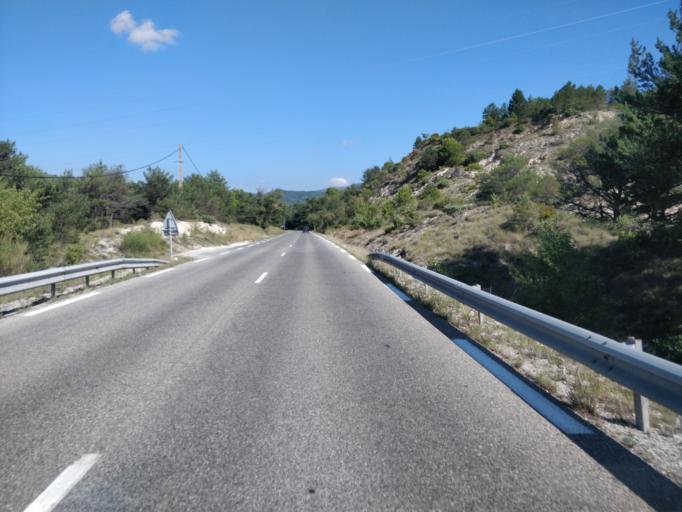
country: FR
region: Provence-Alpes-Cote d'Azur
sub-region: Departement des Alpes-de-Haute-Provence
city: Riez
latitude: 43.8100
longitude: 6.2281
